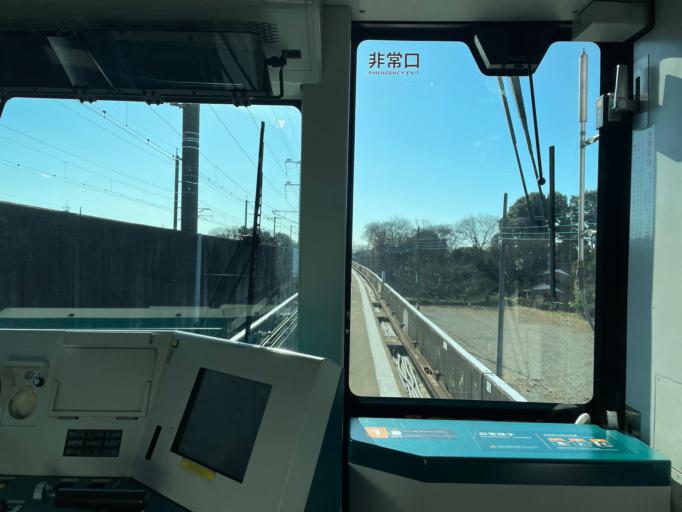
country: JP
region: Saitama
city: Ageoshimo
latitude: 35.9882
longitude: 139.6233
